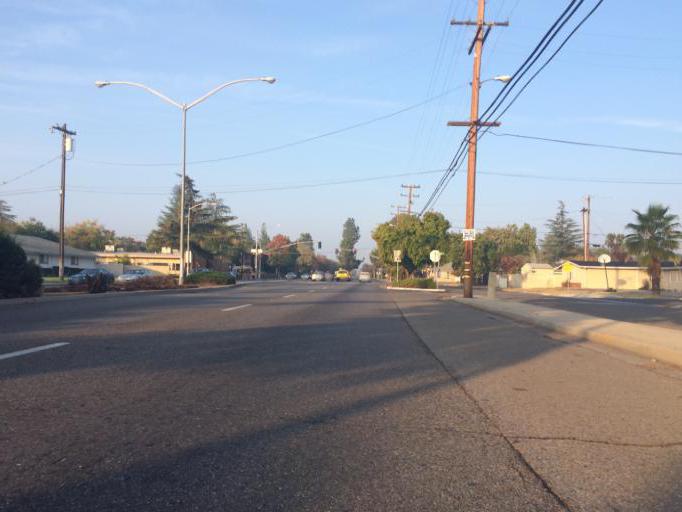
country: US
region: California
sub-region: Fresno County
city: Fresno
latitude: 36.7942
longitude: -119.7619
